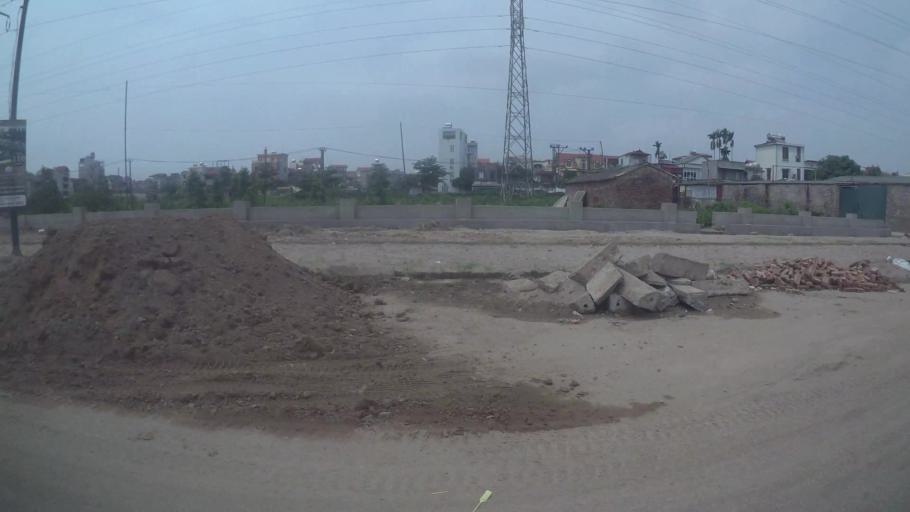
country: VN
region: Ha Noi
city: Tay Ho
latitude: 21.0853
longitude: 105.8016
